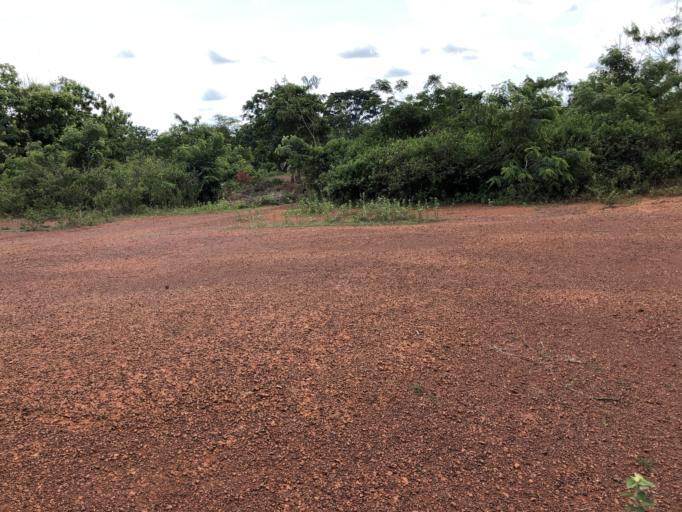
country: CD
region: Equateur
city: Libenge
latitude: 3.7161
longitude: 18.7707
